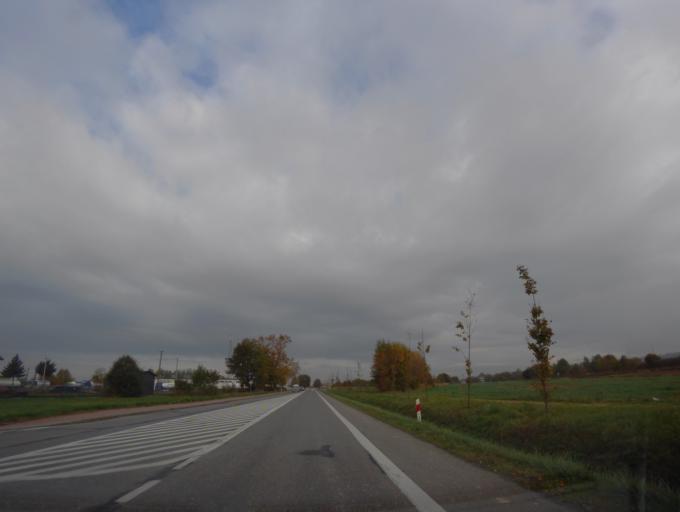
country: PL
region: Lublin Voivodeship
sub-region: Powiat bilgorajski
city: Frampol
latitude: 50.6627
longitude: 22.6757
